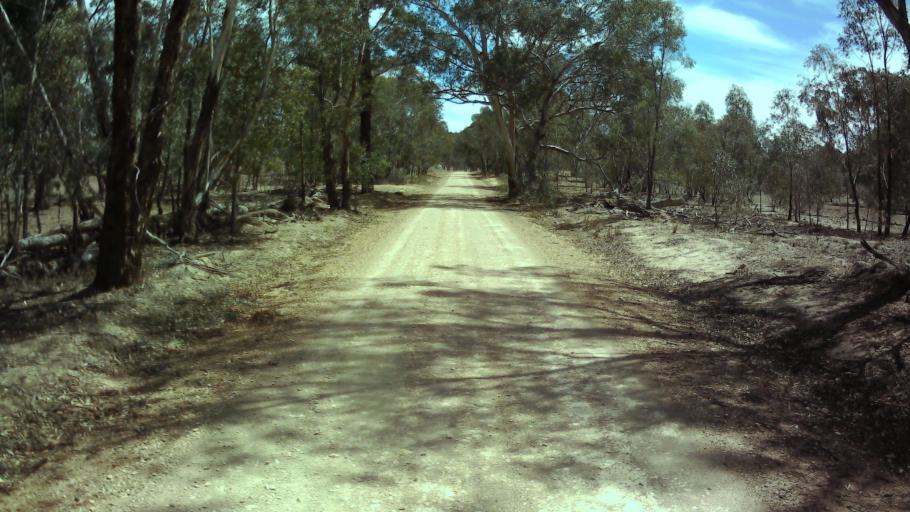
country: AU
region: New South Wales
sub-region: Weddin
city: Grenfell
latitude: -33.7477
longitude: 148.1929
